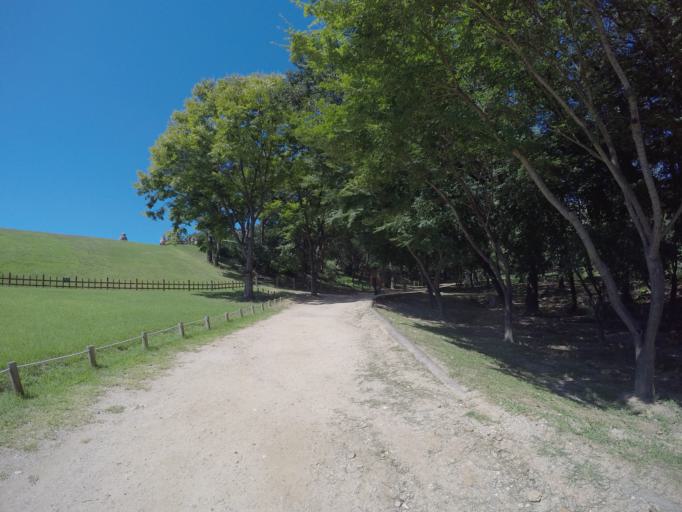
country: KR
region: Seoul
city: Seoul
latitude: 37.5086
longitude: 127.0461
